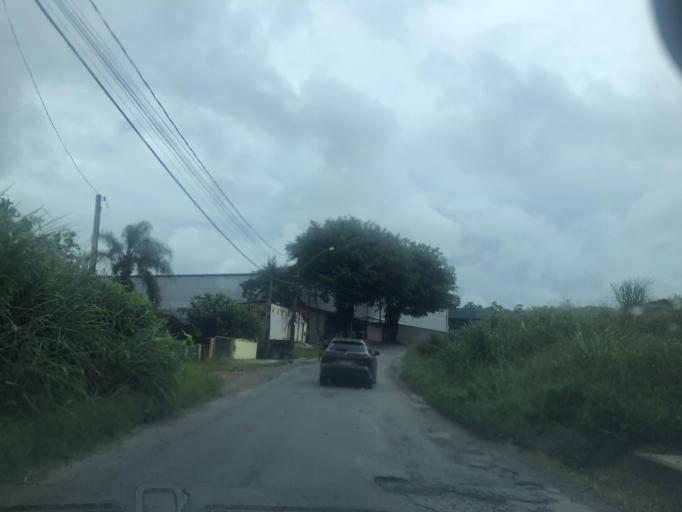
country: BR
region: Santa Catarina
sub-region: Sao Francisco Do Sul
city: Sao Francisco do Sul
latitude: -26.2393
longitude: -48.6161
